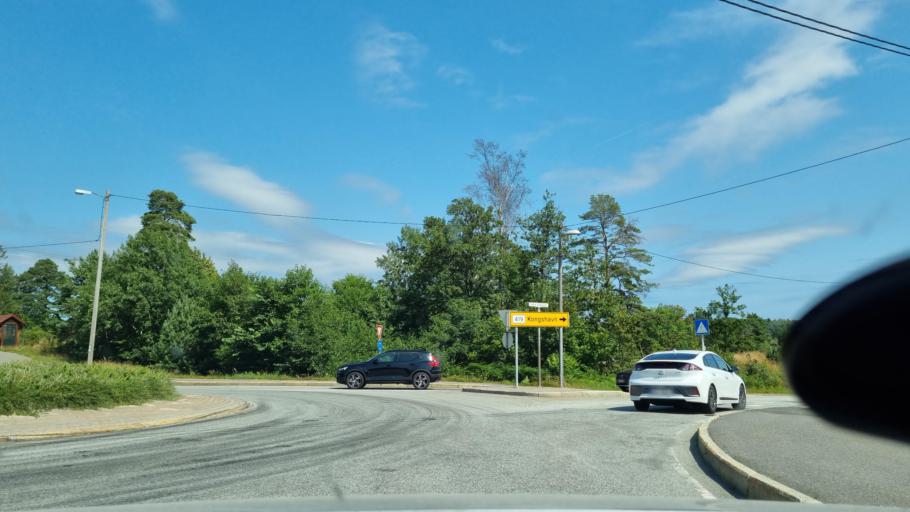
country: NO
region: Aust-Agder
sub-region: Arendal
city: Arendal
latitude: 58.4666
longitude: 8.8247
